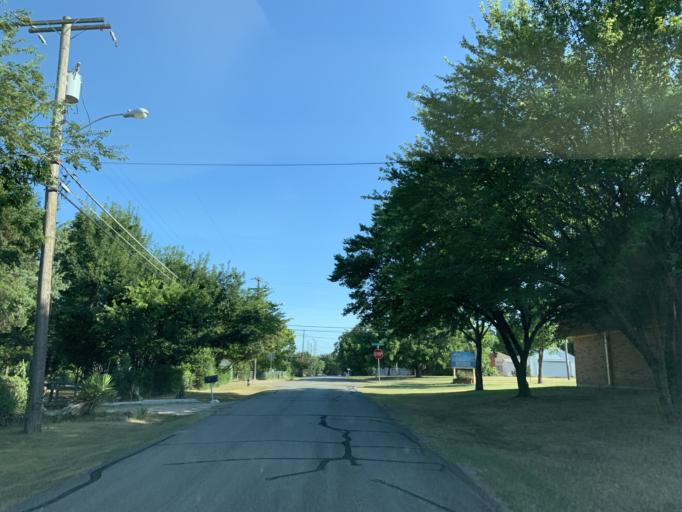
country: US
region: Texas
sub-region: Dallas County
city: Cockrell Hill
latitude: 32.7125
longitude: -96.9044
